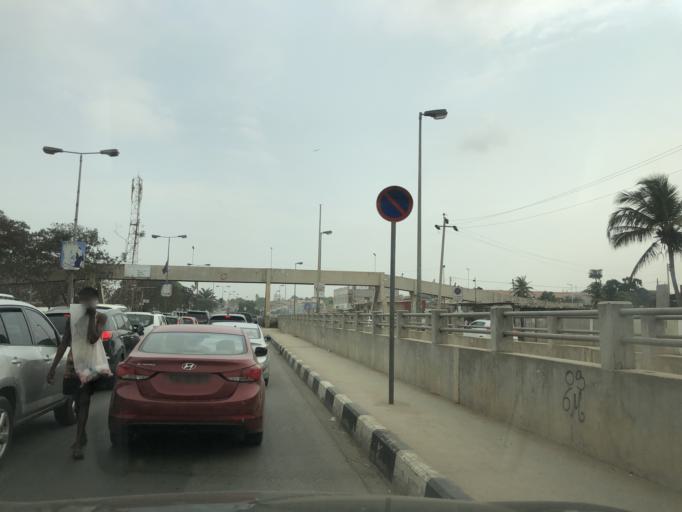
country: AO
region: Luanda
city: Luanda
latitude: -8.8505
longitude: 13.2101
